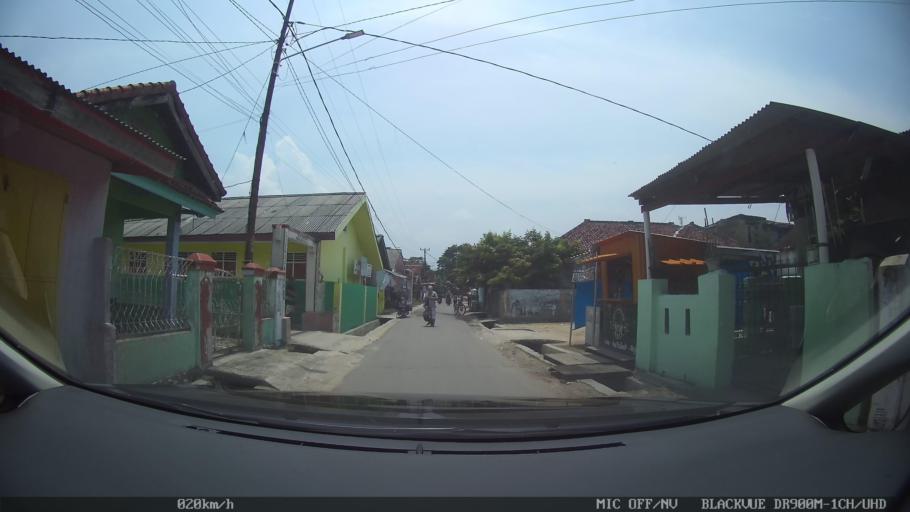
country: ID
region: Lampung
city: Bandarlampung
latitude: -5.4587
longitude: 105.2576
